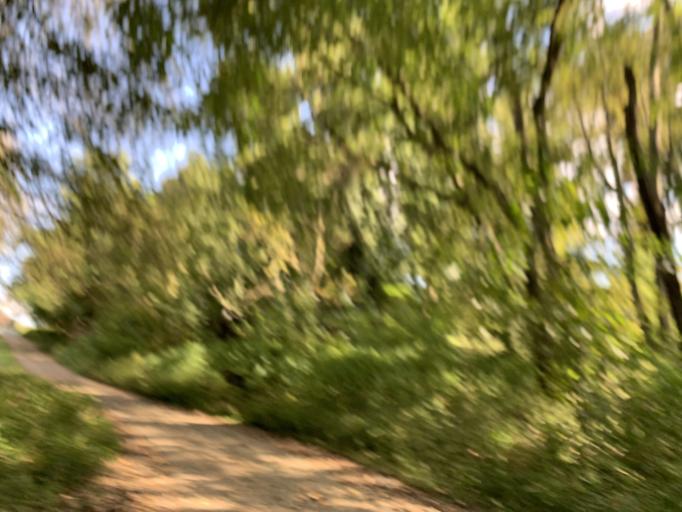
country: US
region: Indiana
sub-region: Floyd County
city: New Albany
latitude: 38.2508
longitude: -85.8328
